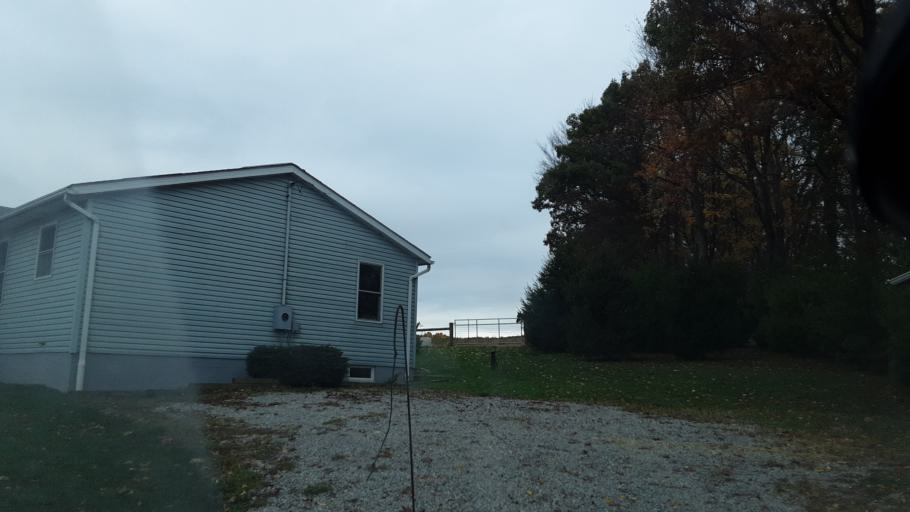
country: US
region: Ohio
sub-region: Knox County
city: Danville
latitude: 40.5440
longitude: -82.3606
